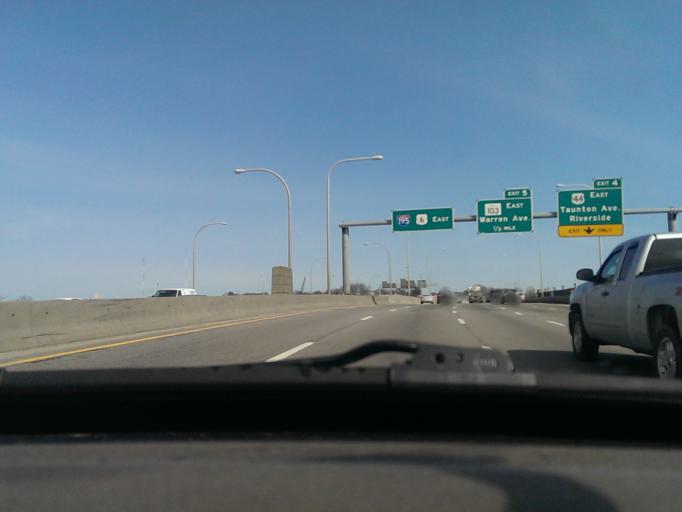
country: US
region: Rhode Island
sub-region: Providence County
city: East Providence
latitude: 41.8191
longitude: -71.3908
